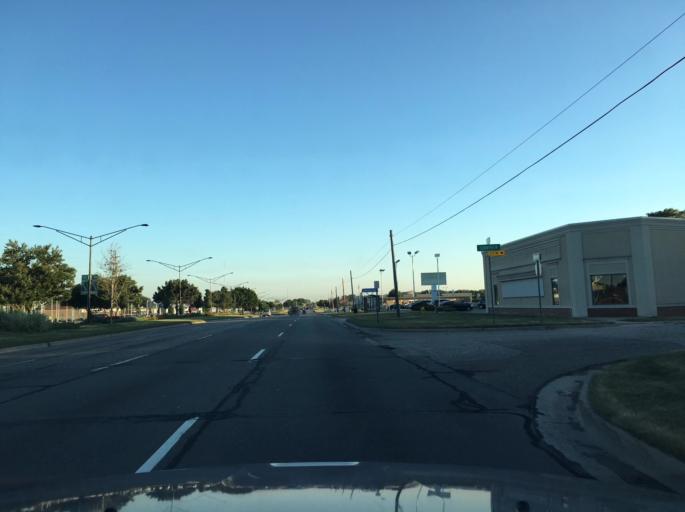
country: US
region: Michigan
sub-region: Macomb County
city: Clinton
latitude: 42.5618
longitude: -82.8961
